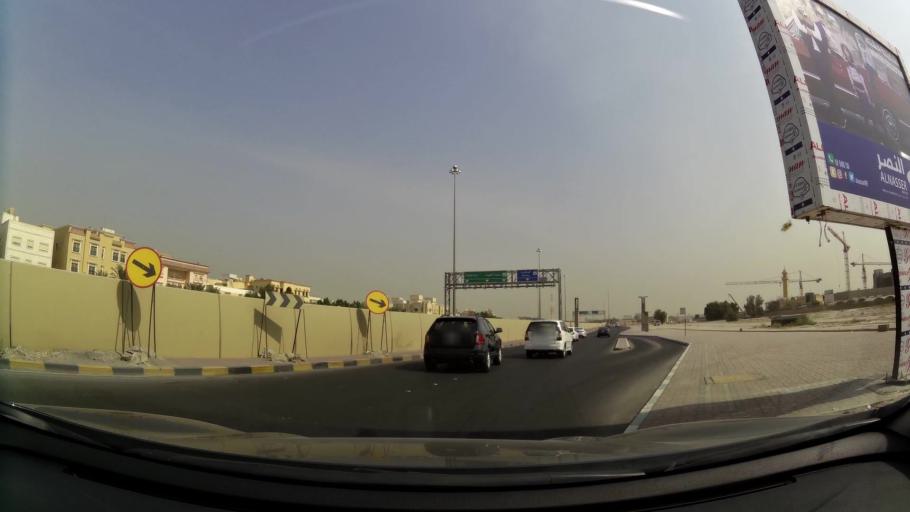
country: KW
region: Al Asimah
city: Ar Rabiyah
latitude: 29.3097
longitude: 47.8754
